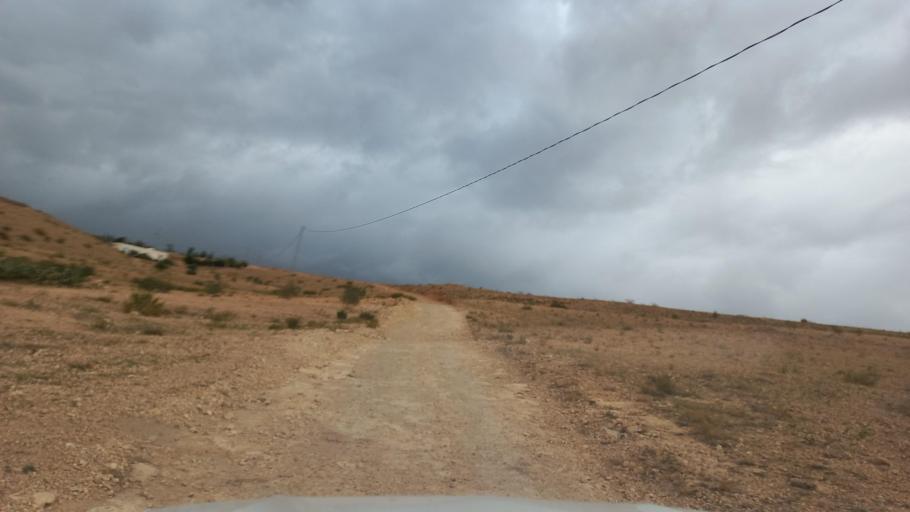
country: TN
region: Al Qasrayn
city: Kasserine
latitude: 35.2764
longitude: 8.9389
